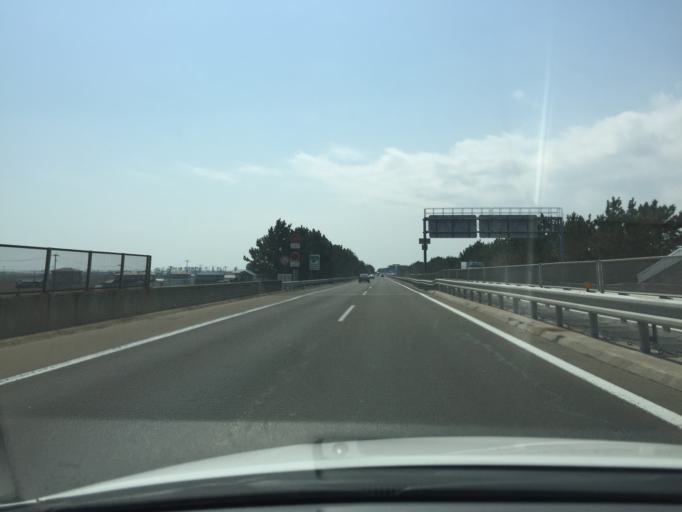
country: JP
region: Miyagi
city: Sendai
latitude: 38.2043
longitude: 140.9439
